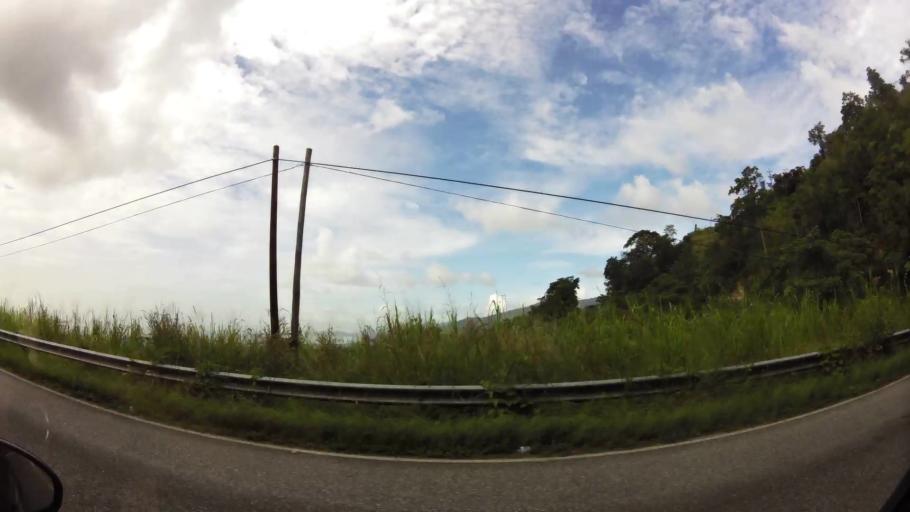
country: TT
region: San Juan/Laventille
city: Laventille
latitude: 10.6734
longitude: -61.4918
